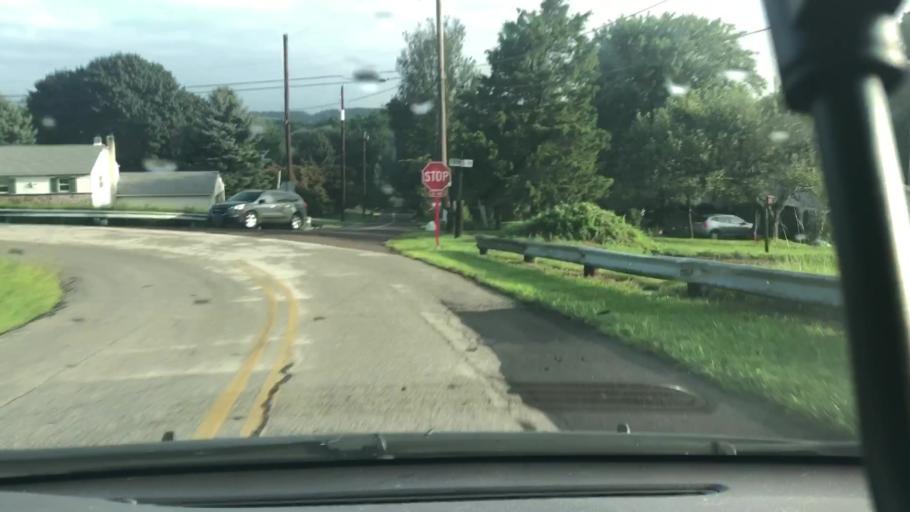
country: US
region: Pennsylvania
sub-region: Chester County
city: Kenilworth
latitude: 40.1805
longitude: -75.6506
